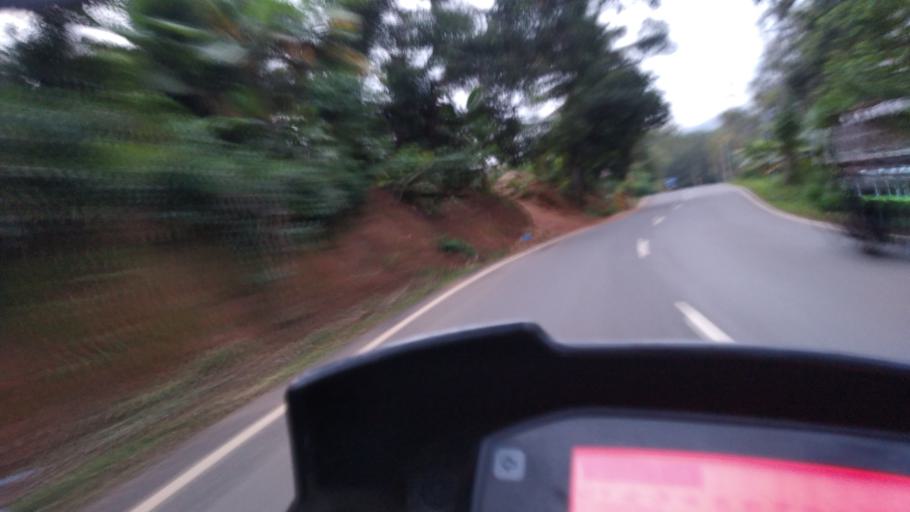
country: IN
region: Kerala
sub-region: Idukki
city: Munnar
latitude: 9.9677
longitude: 77.1342
